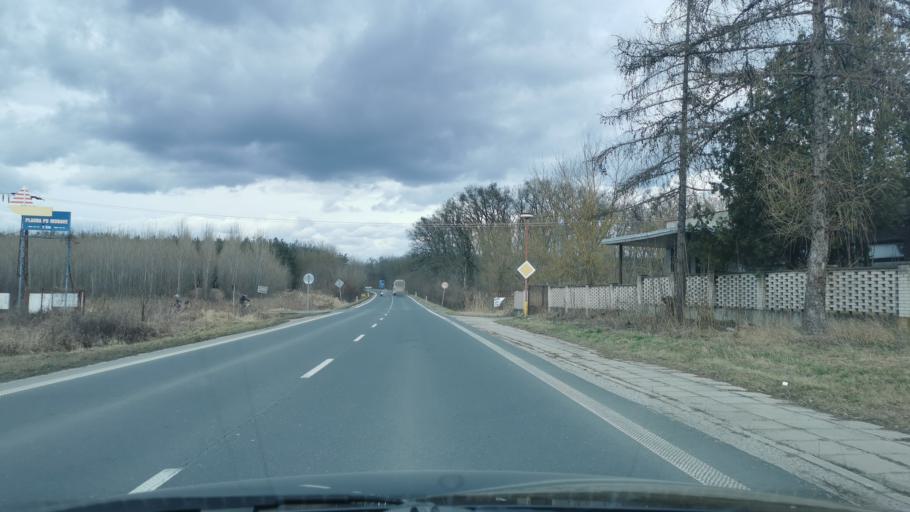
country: CZ
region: South Moravian
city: Tvrdonice
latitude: 48.7239
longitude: 17.0434
